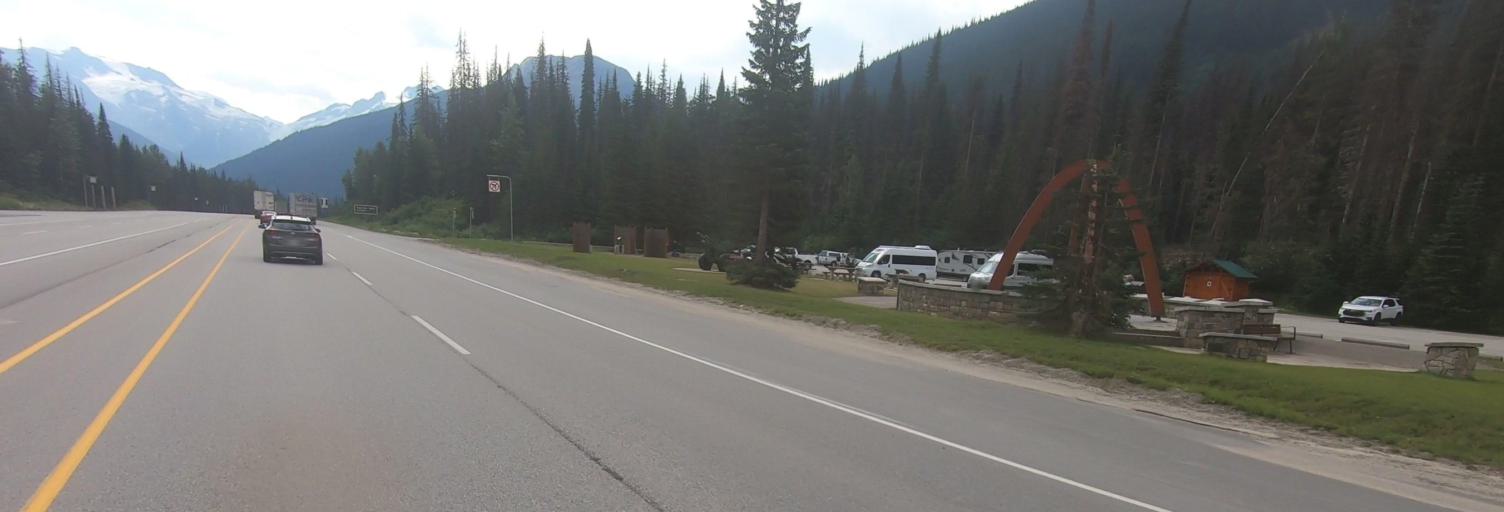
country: CA
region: British Columbia
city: Golden
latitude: 51.2901
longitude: -117.5152
